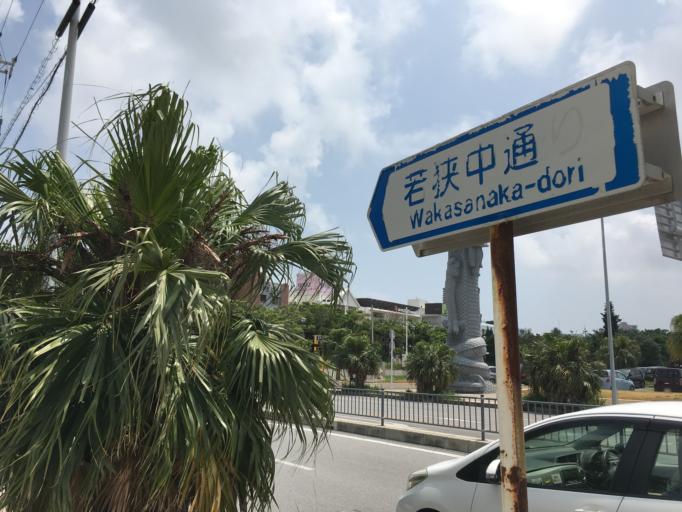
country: JP
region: Okinawa
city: Naha-shi
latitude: 26.2226
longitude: 127.6739
